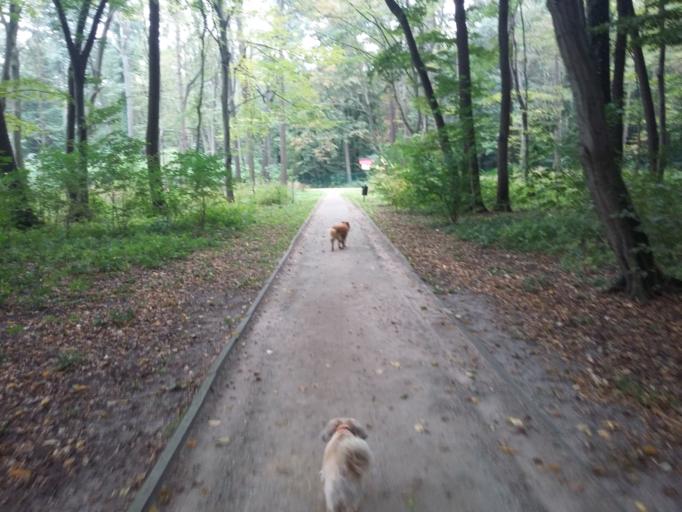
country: PL
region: Lodz Voivodeship
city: Lodz
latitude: 51.7591
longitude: 19.4225
